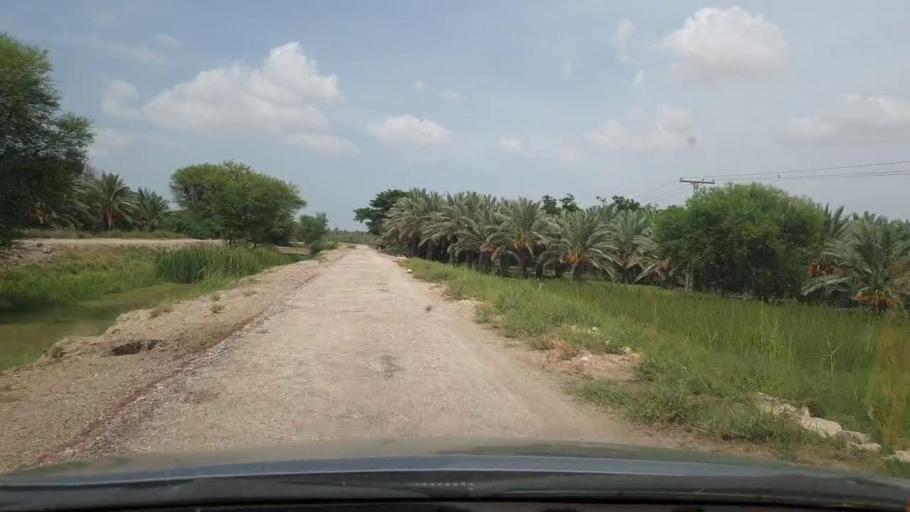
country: PK
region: Sindh
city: Khairpur
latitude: 27.5129
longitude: 68.8784
